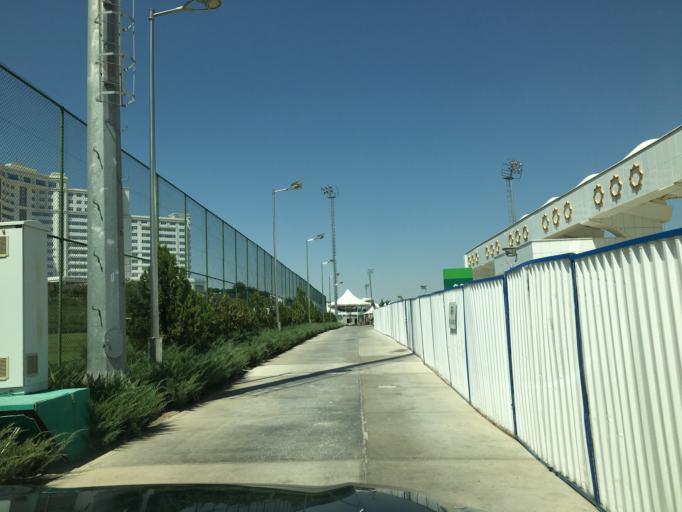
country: TM
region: Ahal
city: Ashgabat
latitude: 37.9267
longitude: 58.3473
